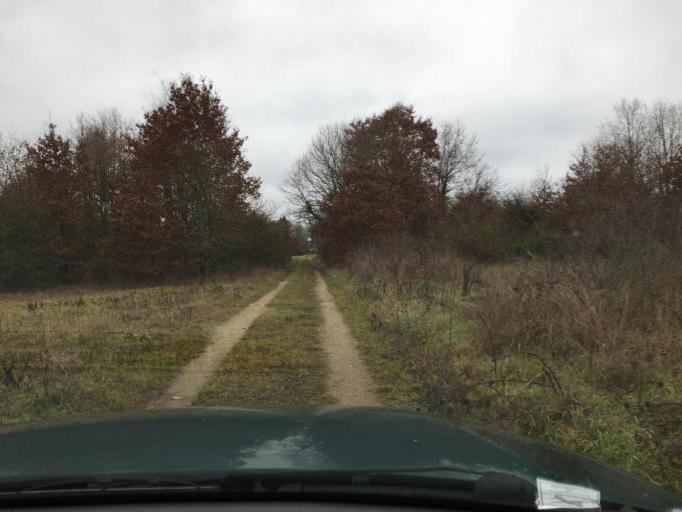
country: FR
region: Centre
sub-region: Departement du Loiret
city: Olivet
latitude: 47.8536
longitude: 1.8790
